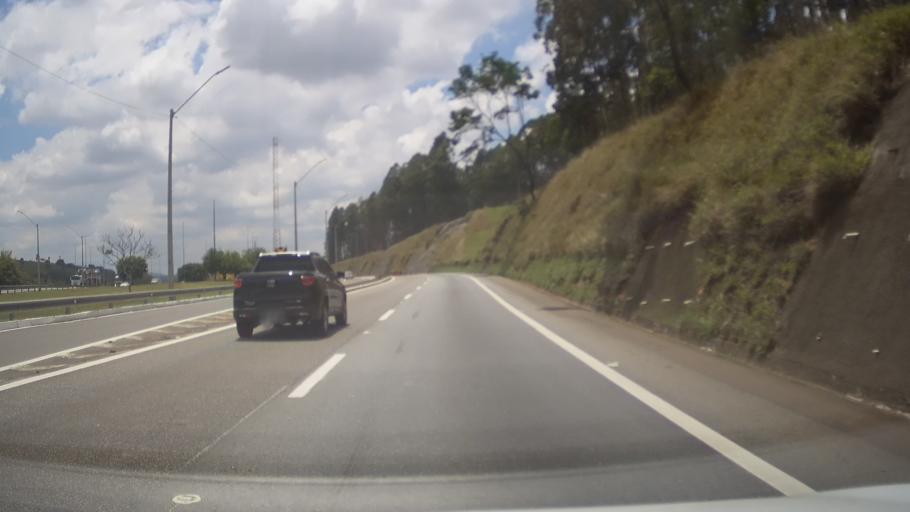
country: BR
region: Minas Gerais
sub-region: Tres Coracoes
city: Tres Coracoes
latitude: -21.6918
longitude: -45.3508
